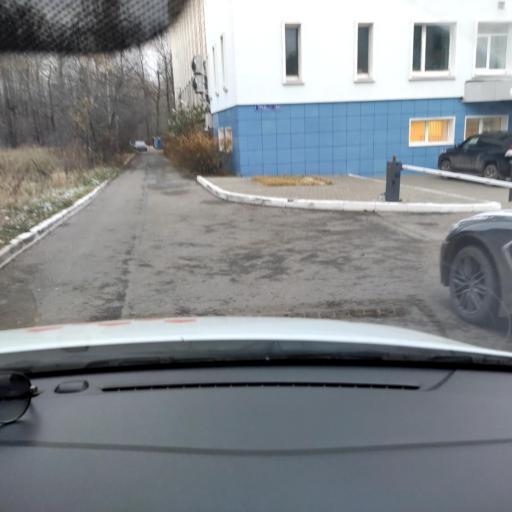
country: RU
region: Tatarstan
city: Vysokaya Gora
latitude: 55.8585
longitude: 49.2229
